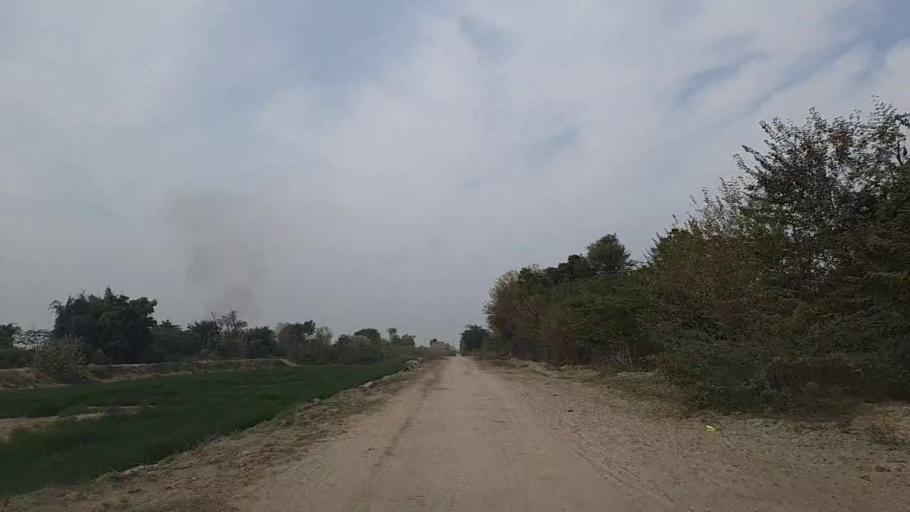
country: PK
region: Sindh
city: Daur
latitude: 26.4457
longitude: 68.4542
